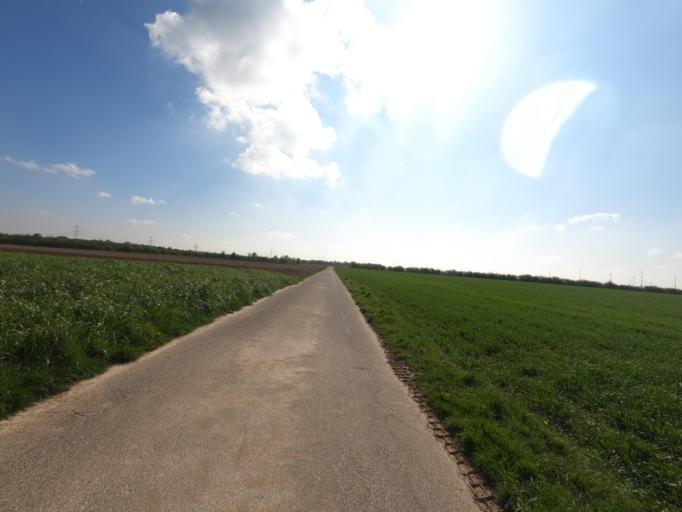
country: DE
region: North Rhine-Westphalia
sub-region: Regierungsbezirk Koln
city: Heinsberg
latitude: 51.0475
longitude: 6.0793
